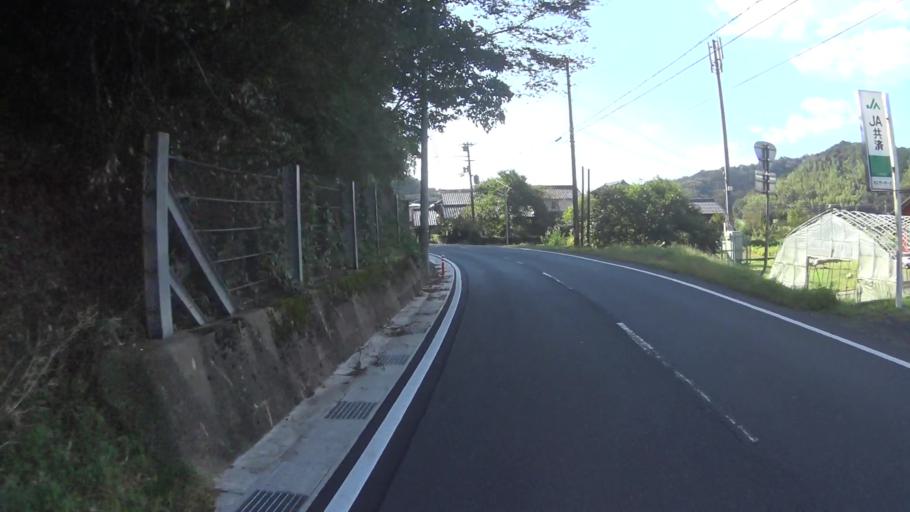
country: JP
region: Kyoto
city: Miyazu
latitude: 35.7096
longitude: 135.1058
